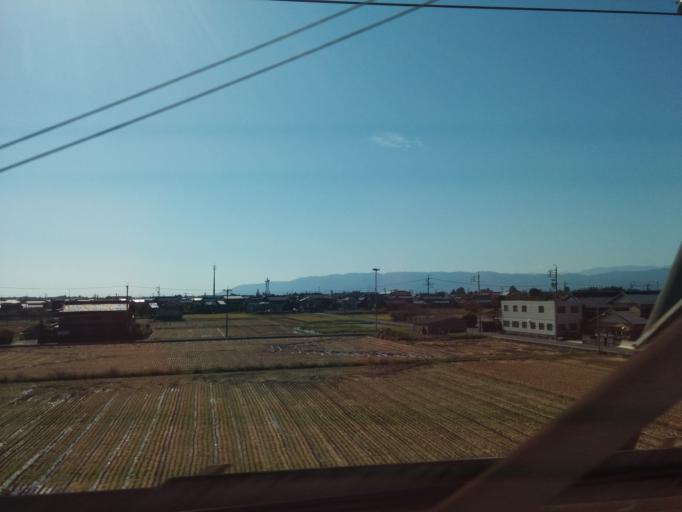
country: JP
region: Aichi
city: Sobue
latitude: 35.3031
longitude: 136.7059
